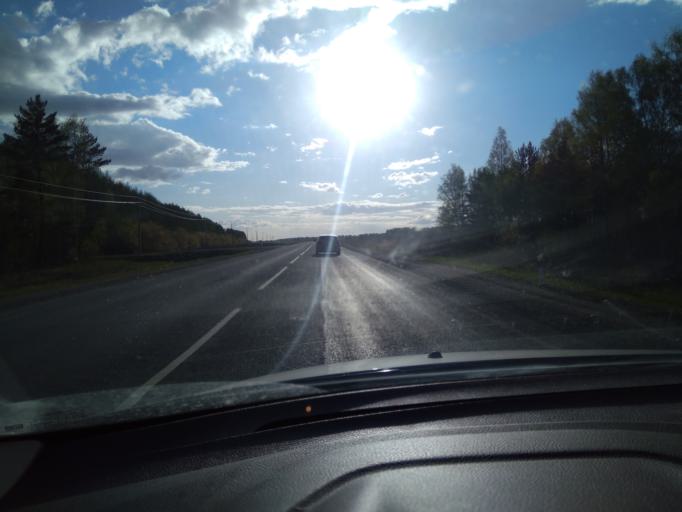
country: RU
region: Sverdlovsk
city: Troitskiy
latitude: 57.0912
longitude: 63.8081
